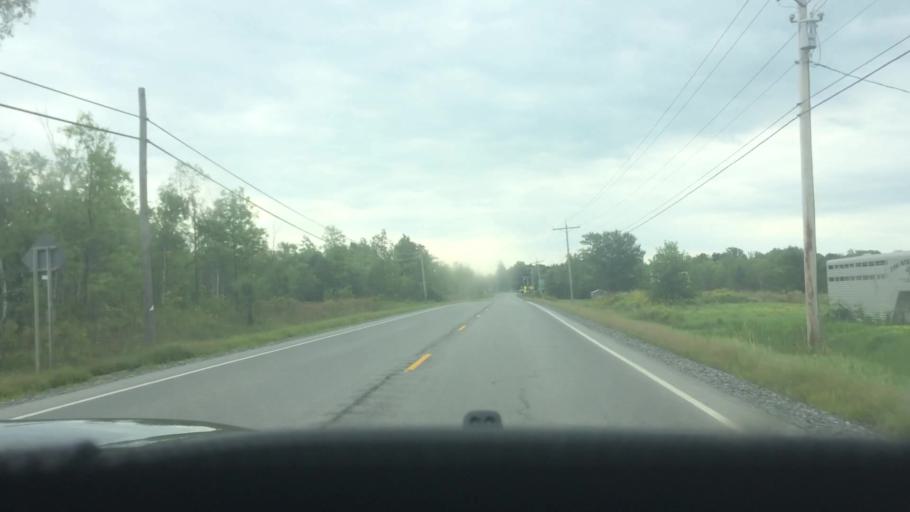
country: US
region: New York
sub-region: St. Lawrence County
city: Ogdensburg
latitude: 44.6259
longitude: -75.4171
